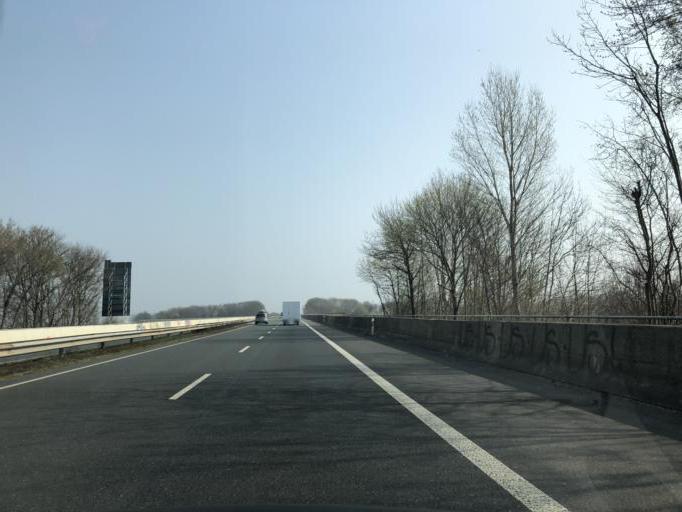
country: DE
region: North Rhine-Westphalia
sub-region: Regierungsbezirk Detmold
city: Minden
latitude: 52.2693
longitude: 8.9234
